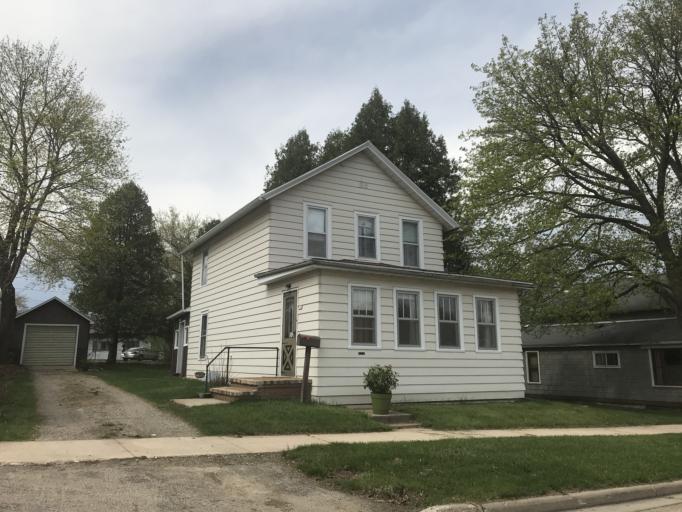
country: US
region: Wisconsin
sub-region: Oconto County
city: Oconto Falls
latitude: 44.8716
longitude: -88.1460
